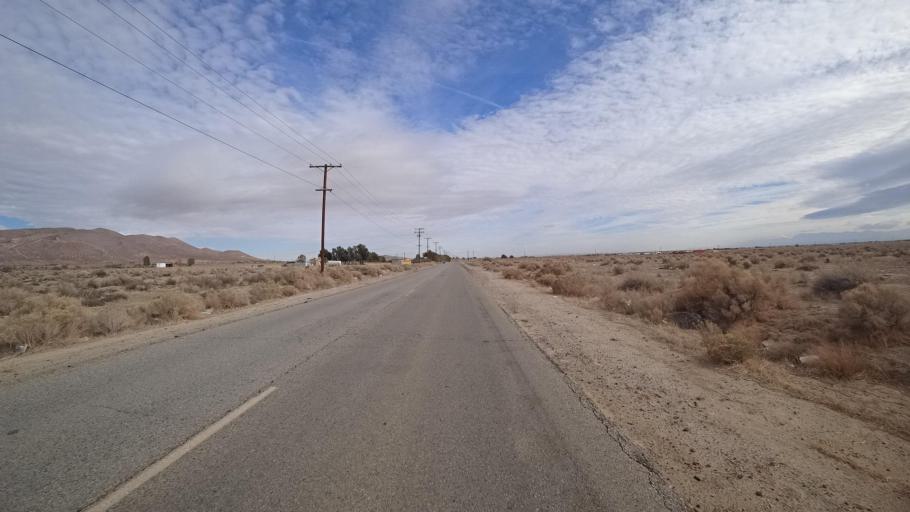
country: US
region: California
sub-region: Kern County
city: Rosamond
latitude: 34.8636
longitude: -118.2965
